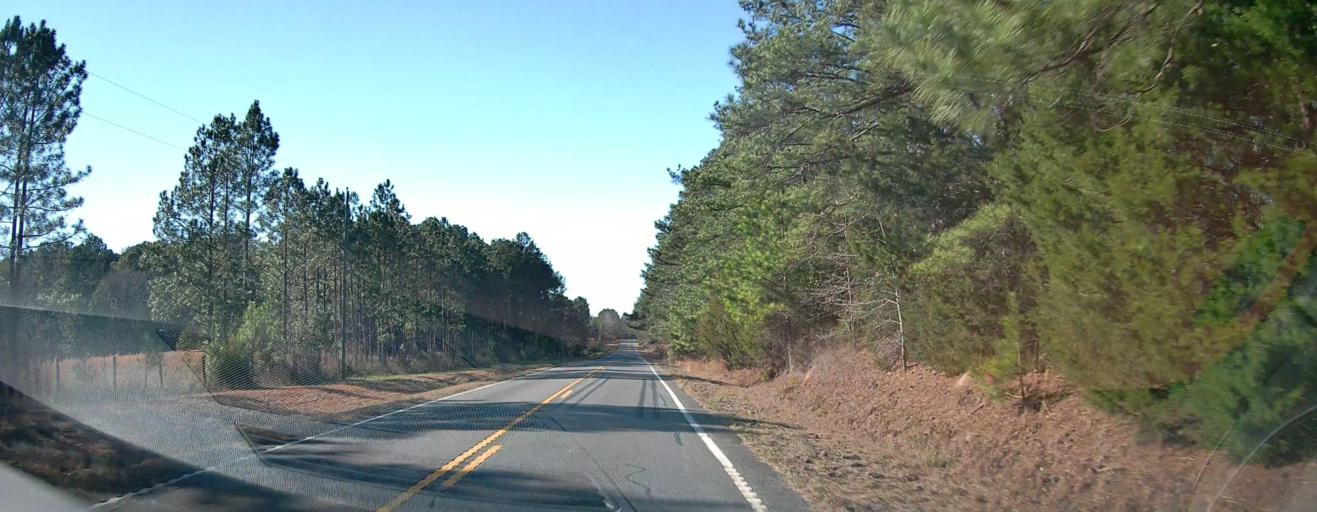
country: US
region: Georgia
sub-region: Talbot County
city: Talbotton
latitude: 32.6464
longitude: -84.4384
